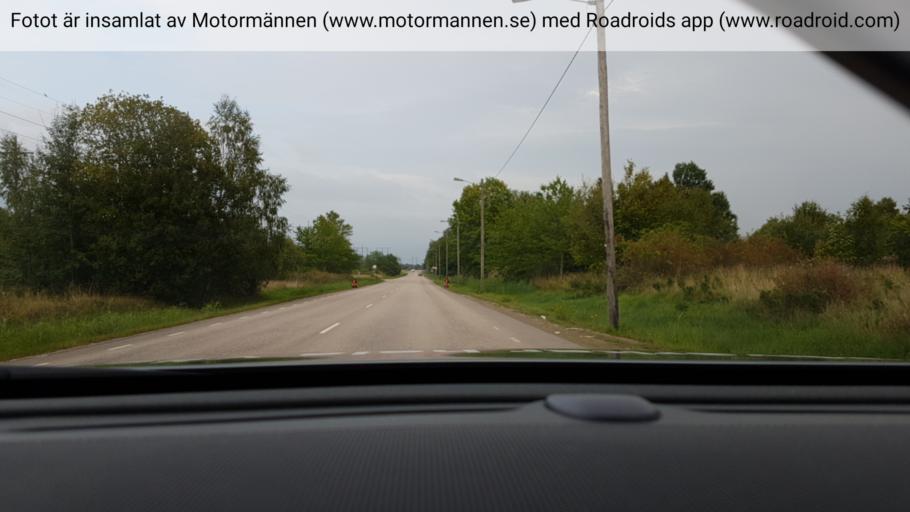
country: SE
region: Vaestra Goetaland
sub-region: Vanersborgs Kommun
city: Vanersborg
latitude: 58.3586
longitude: 12.3361
